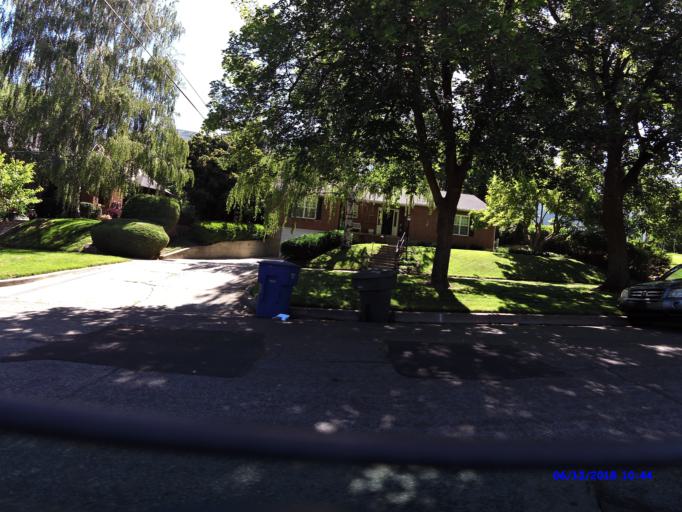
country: US
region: Utah
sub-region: Weber County
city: Ogden
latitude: 41.2176
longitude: -111.9401
